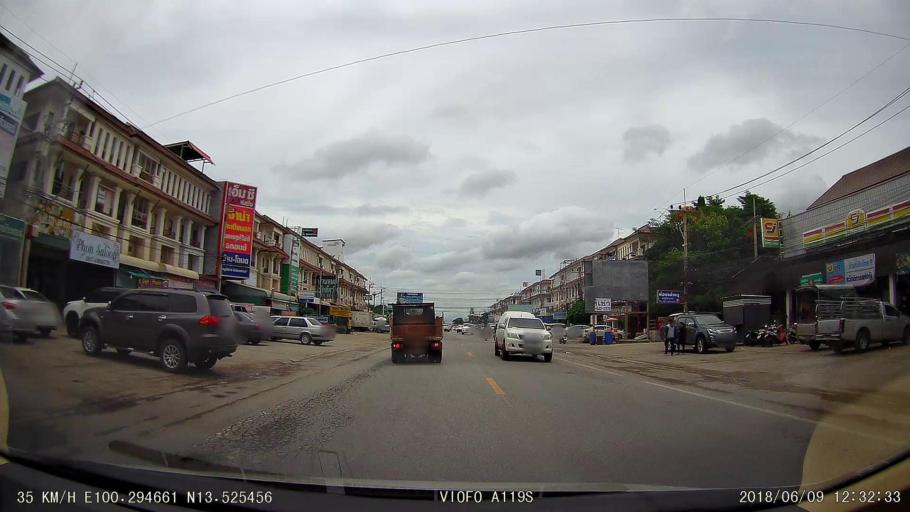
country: TH
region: Samut Sakhon
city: Samut Sakhon
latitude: 13.5254
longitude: 100.2947
